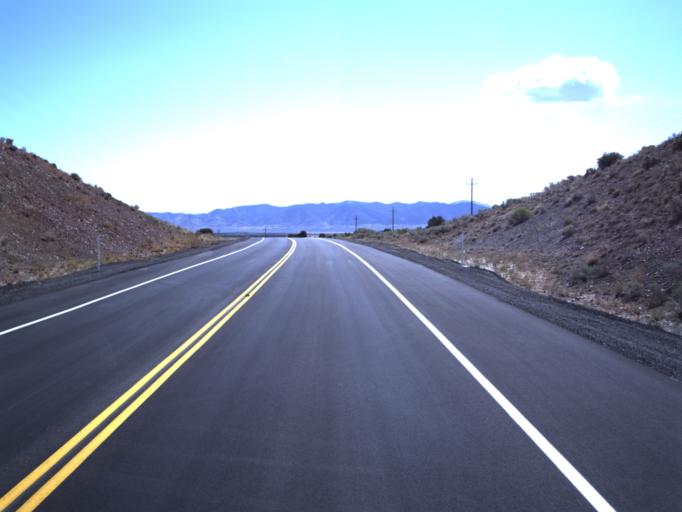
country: US
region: Utah
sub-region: Utah County
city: Eagle Mountain
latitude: 40.0721
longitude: -112.3720
